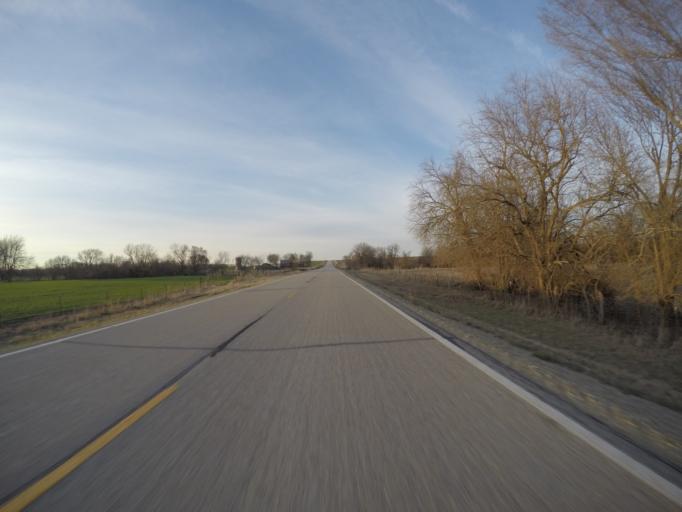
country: US
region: Kansas
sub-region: Riley County
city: Fort Riley North
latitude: 39.3833
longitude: -96.8493
